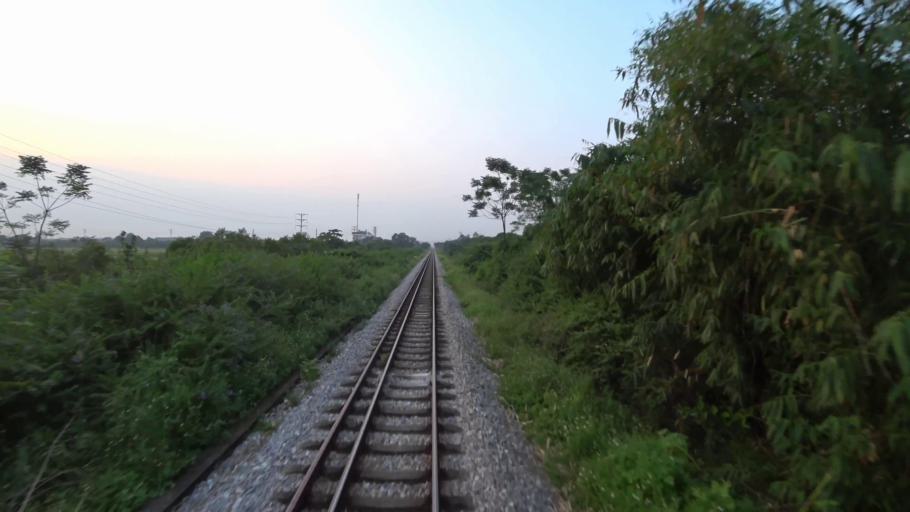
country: VN
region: Ha Noi
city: Dong Anh
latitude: 21.1253
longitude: 105.8812
